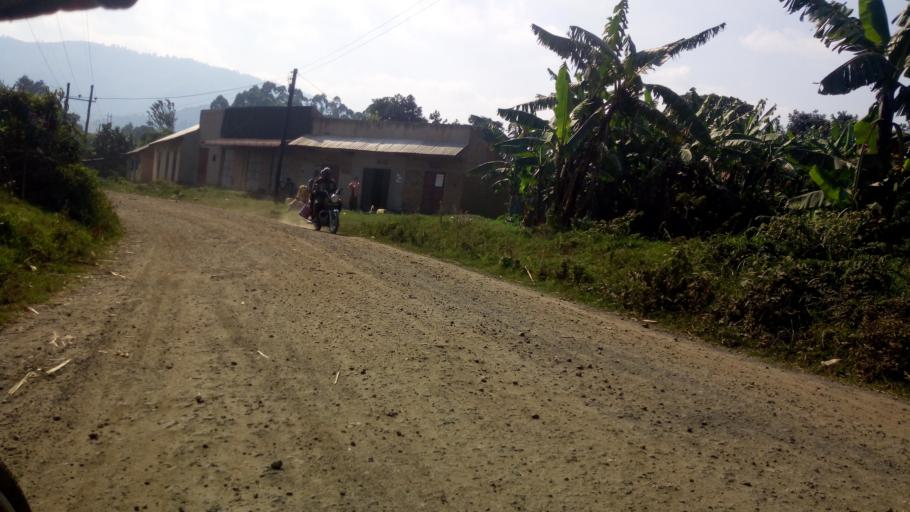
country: UG
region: Western Region
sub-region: Kisoro District
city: Kisoro
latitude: -1.2251
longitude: 29.7149
